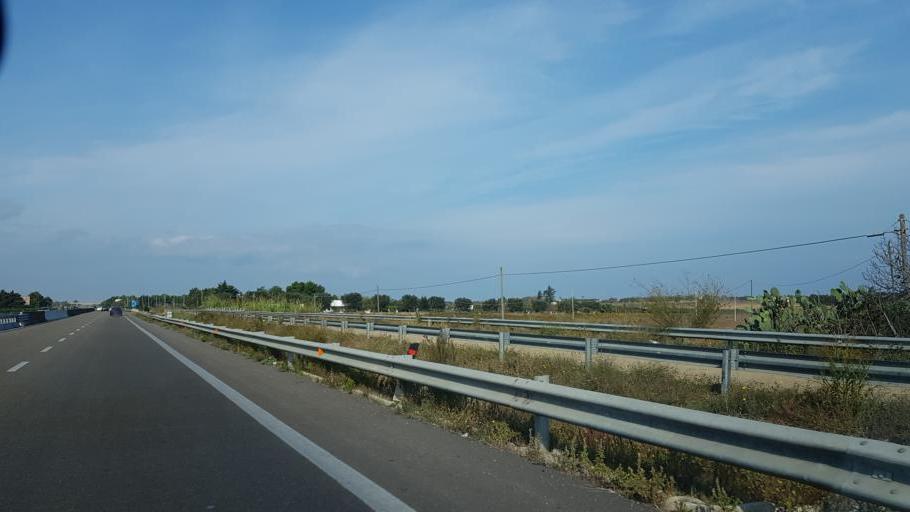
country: IT
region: Apulia
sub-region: Provincia di Brindisi
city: Brindisi
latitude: 40.6813
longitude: 17.8385
